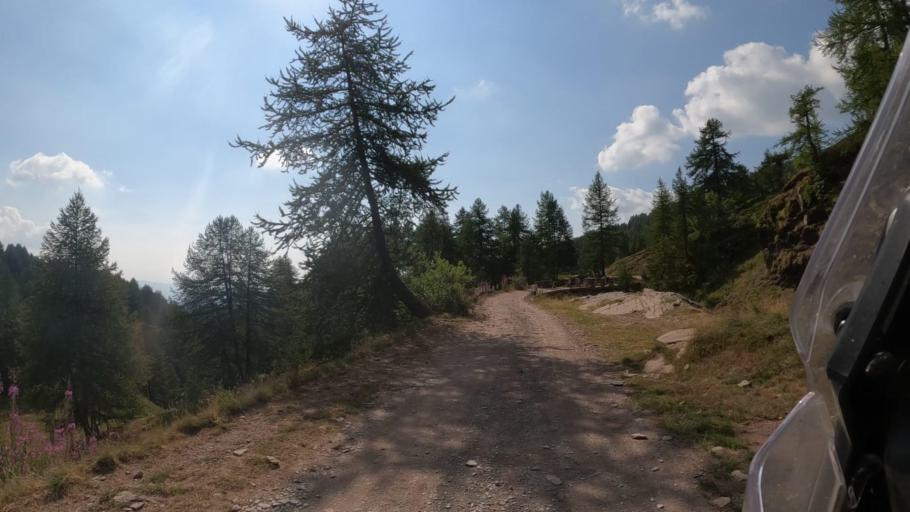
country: IT
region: Piedmont
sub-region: Provincia di Cuneo
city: Briga Alta
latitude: 44.1171
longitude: 7.6981
